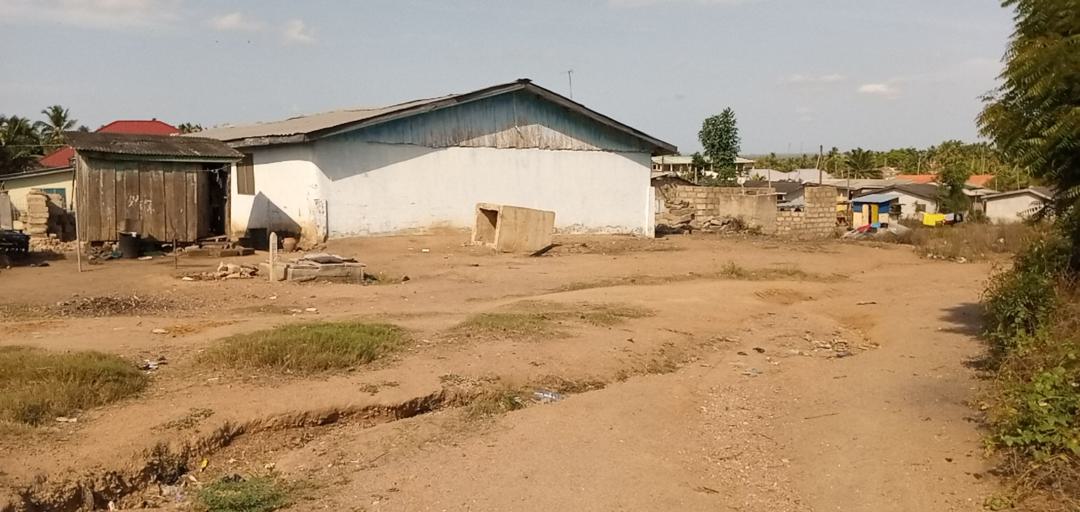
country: GH
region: Central
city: Winneba
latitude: 5.3529
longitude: -0.6217
